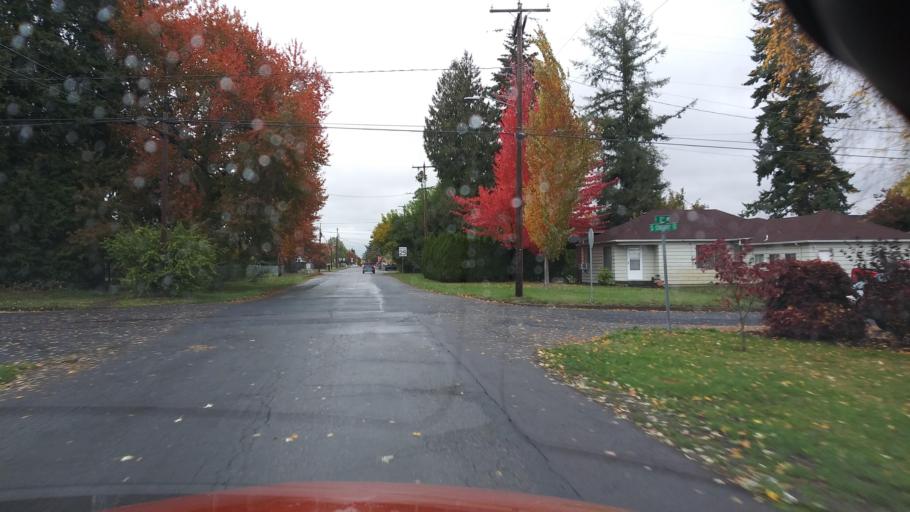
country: US
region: Oregon
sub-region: Washington County
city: Cornelius
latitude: 45.5173
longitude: -123.0570
